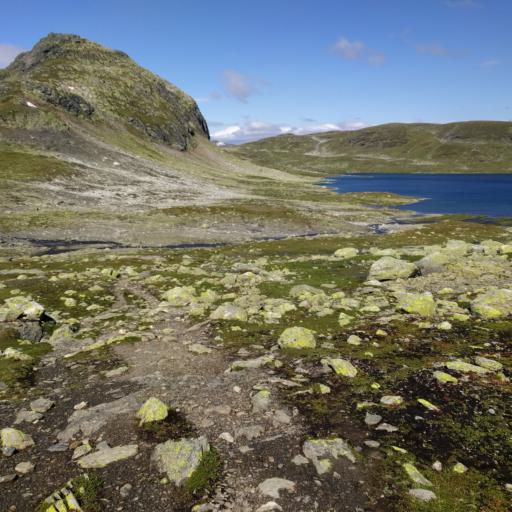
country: NO
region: Aust-Agder
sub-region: Bykle
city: Hovden
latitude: 59.8670
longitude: 7.2162
